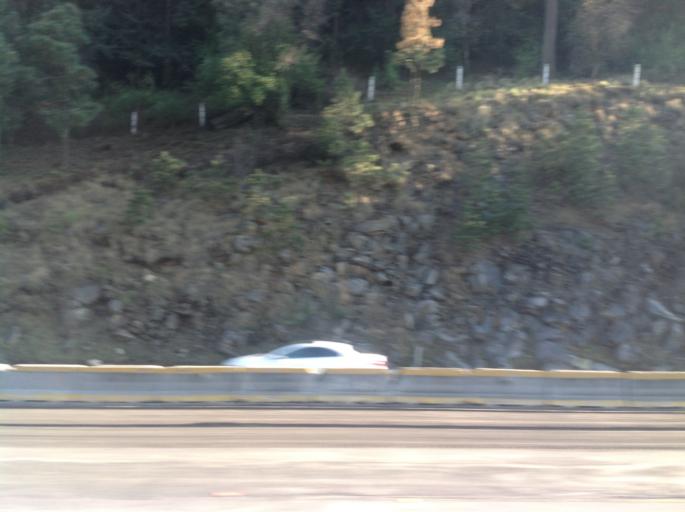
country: MX
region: Mexico
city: Rio Frio de Juarez
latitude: 19.3365
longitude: -98.7096
